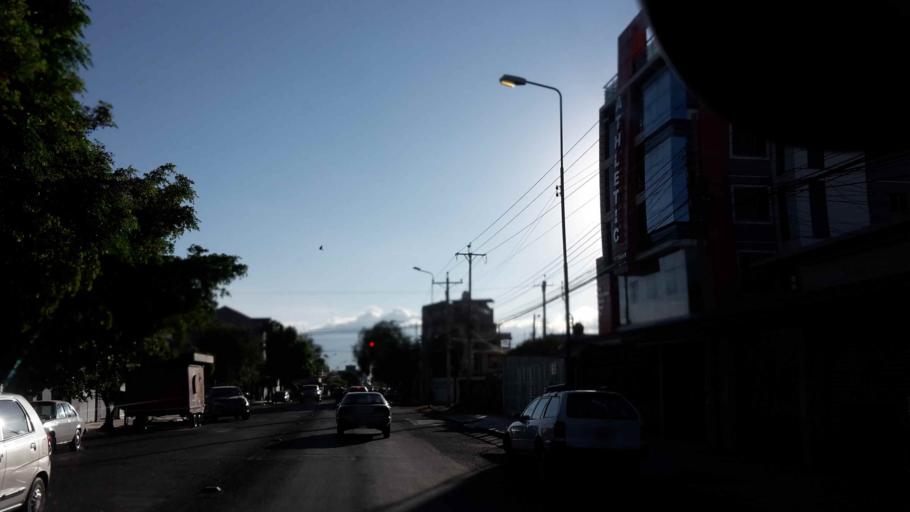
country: BO
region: Cochabamba
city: Cochabamba
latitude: -17.3882
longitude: -66.1732
